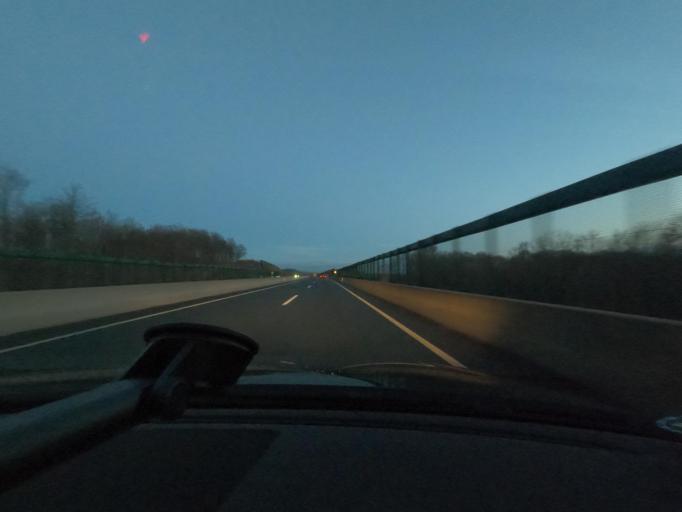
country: DE
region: Lower Saxony
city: Bad Lauterberg im Harz
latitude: 51.6134
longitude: 10.4494
